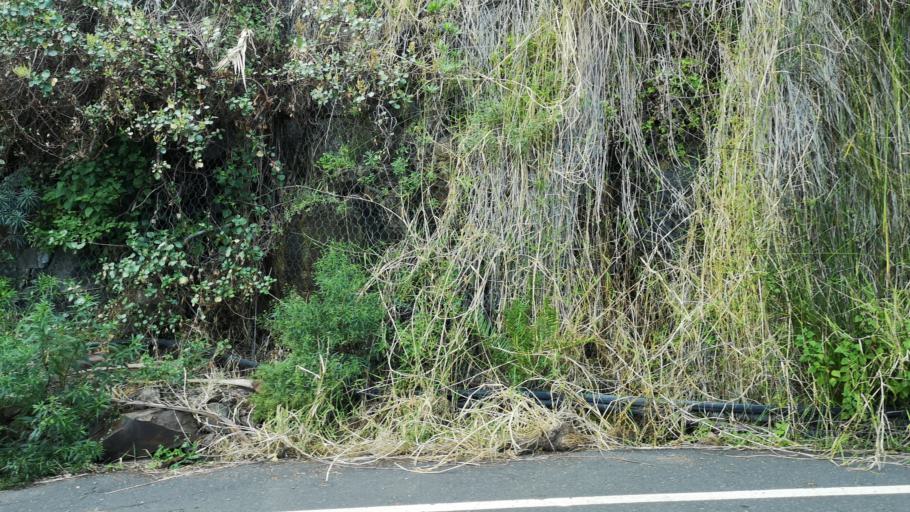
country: ES
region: Canary Islands
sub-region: Provincia de Santa Cruz de Tenerife
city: Agulo
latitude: 28.1898
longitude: -17.1984
